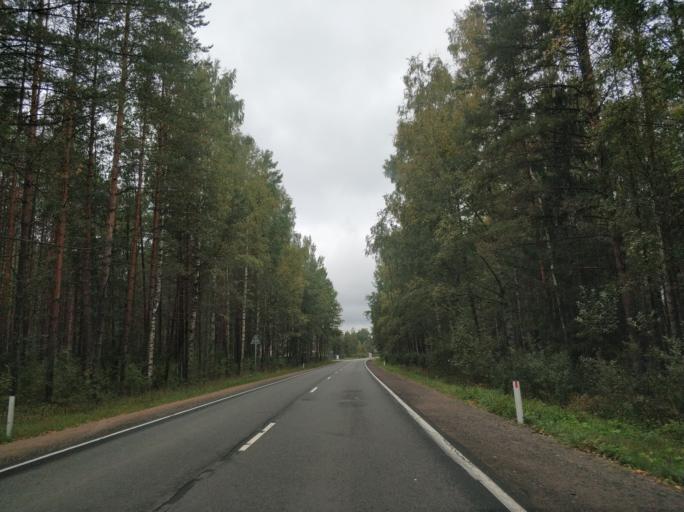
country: RU
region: Leningrad
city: Borisova Griva
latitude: 60.0910
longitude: 30.8582
